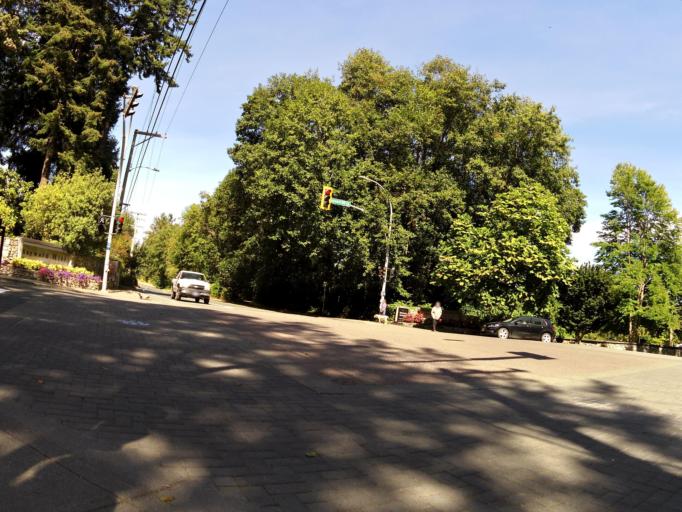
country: CA
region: British Columbia
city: Victoria
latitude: 48.5299
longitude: -123.3742
